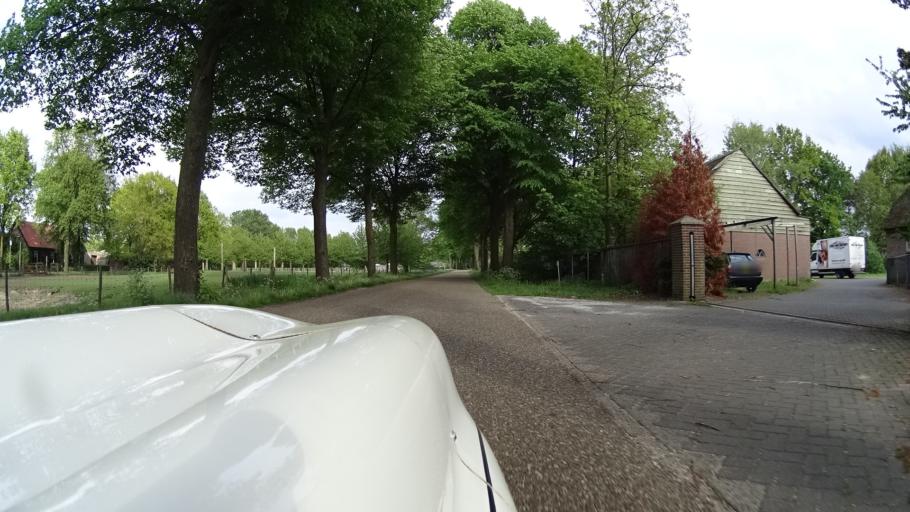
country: NL
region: North Brabant
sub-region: Gemeente Uden
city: Volkel
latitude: 51.6349
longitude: 5.6683
